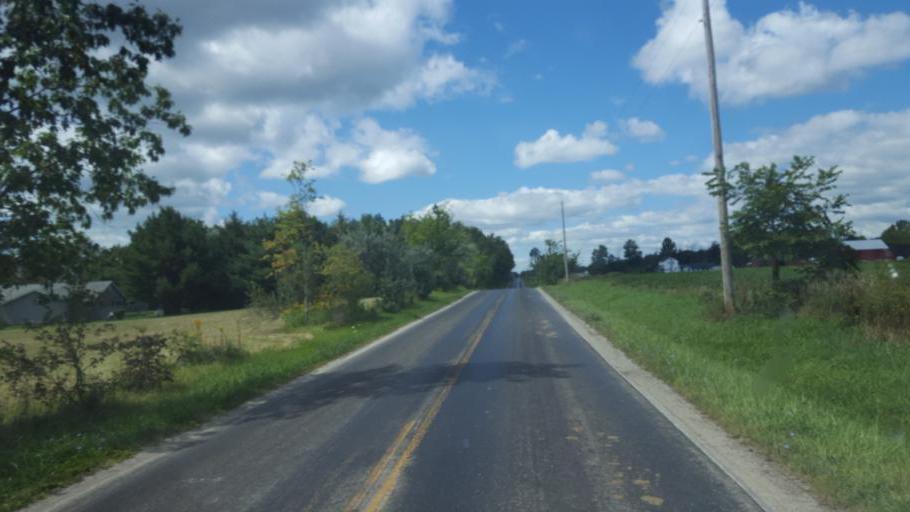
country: US
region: Ohio
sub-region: Wayne County
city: West Salem
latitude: 40.9921
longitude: -82.1968
